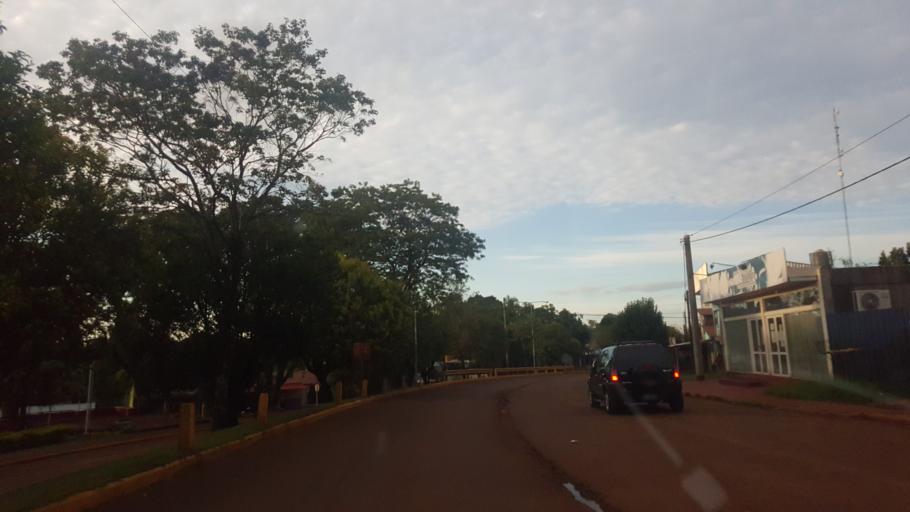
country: AR
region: Misiones
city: Dos de Mayo
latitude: -27.0241
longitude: -54.6861
